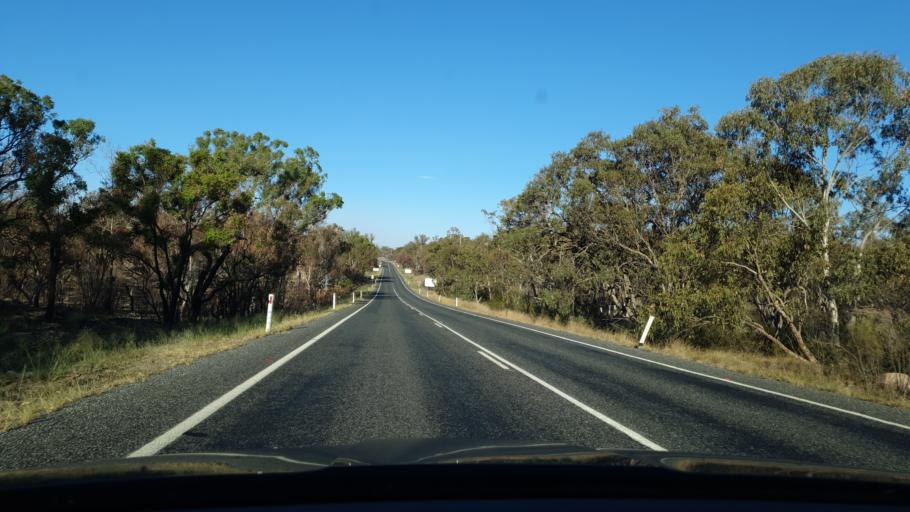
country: AU
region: Queensland
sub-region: Southern Downs
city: Stanthorpe
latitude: -28.6405
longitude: 151.9406
